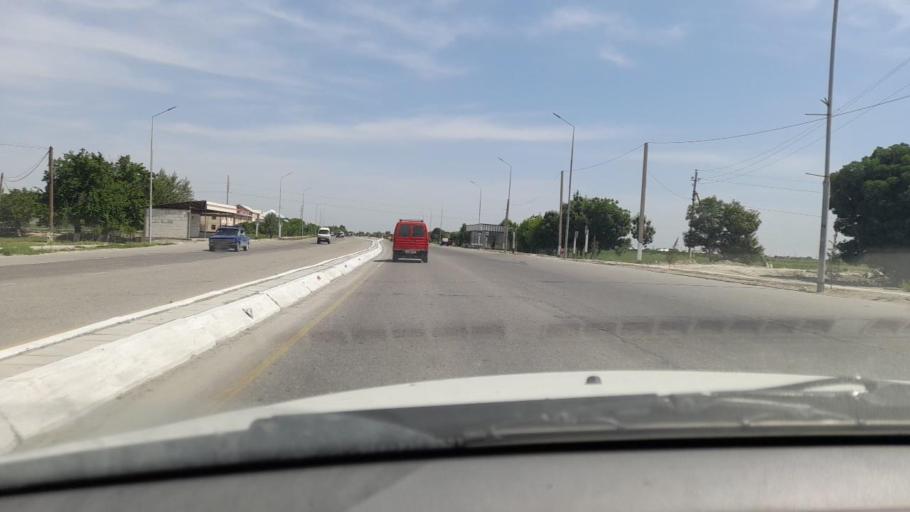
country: UZ
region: Bukhara
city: Galaosiyo
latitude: 39.8658
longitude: 64.4493
